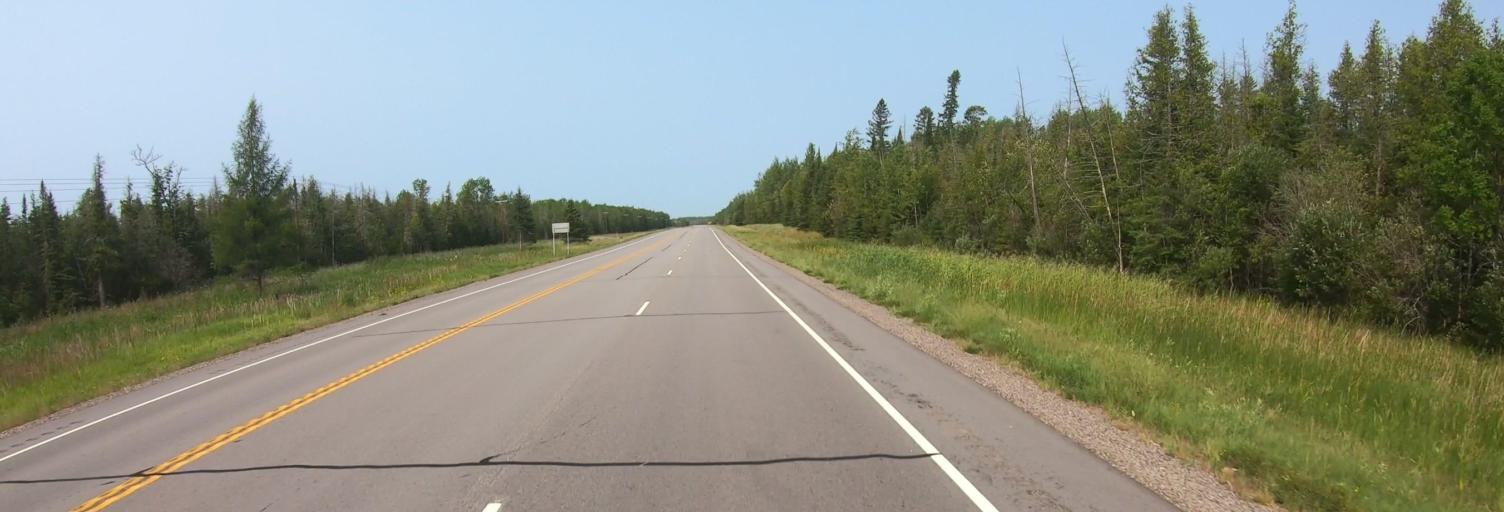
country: CA
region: Ontario
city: Fort Frances
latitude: 48.4032
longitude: -93.0269
